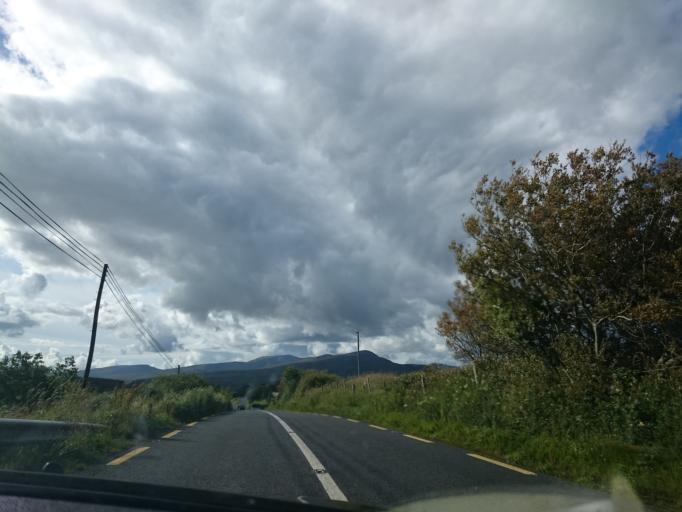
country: IE
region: Connaught
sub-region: Maigh Eo
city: Westport
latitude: 53.8967
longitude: -9.5576
